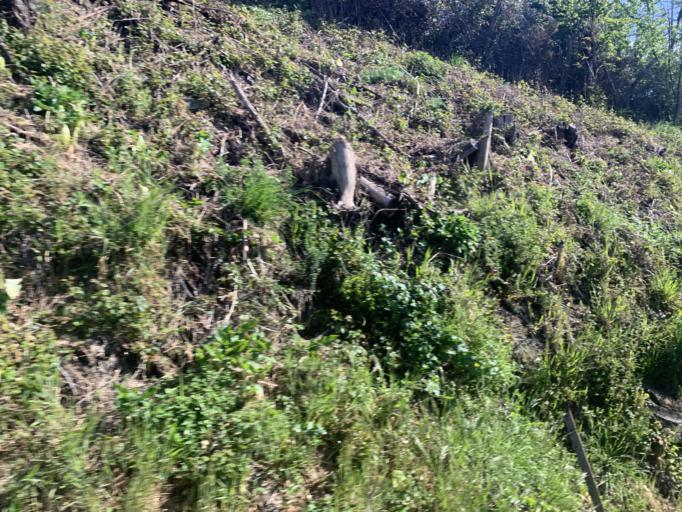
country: IT
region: Latium
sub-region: Citta metropolitana di Roma Capitale
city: Castel Gandolfo
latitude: 41.7694
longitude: 12.6509
